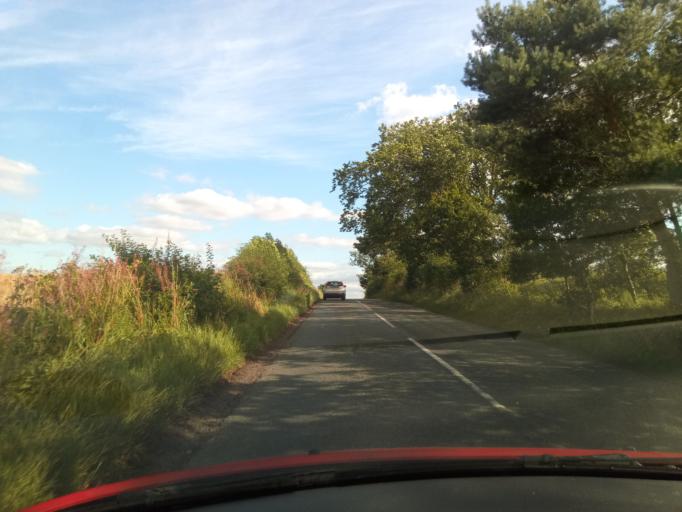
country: GB
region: Scotland
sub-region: The Scottish Borders
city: Coldstream
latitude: 55.7127
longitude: -2.2817
